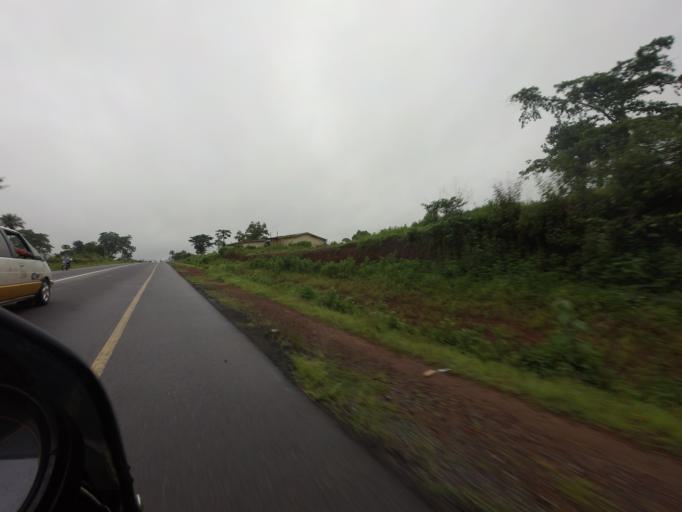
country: SL
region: Northern Province
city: Kambia
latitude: 9.0652
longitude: -12.9160
